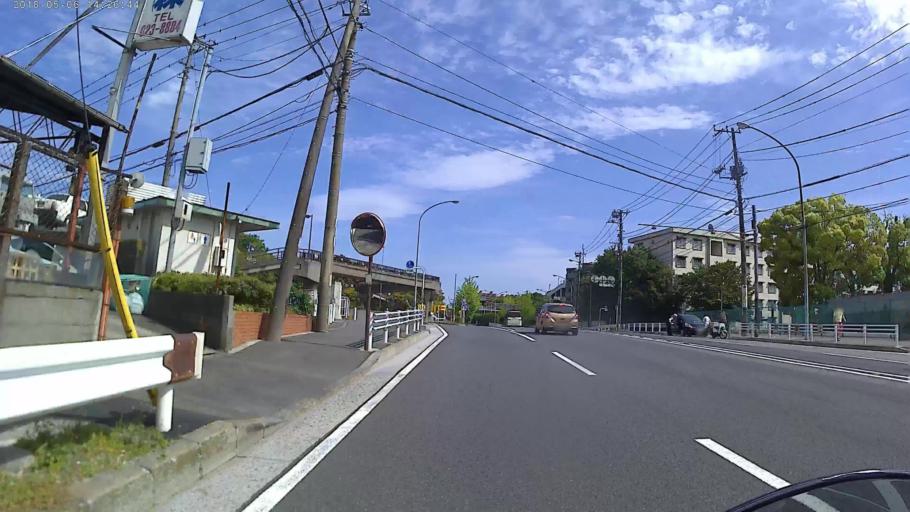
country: JP
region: Kanagawa
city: Yokohama
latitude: 35.4330
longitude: 139.6641
